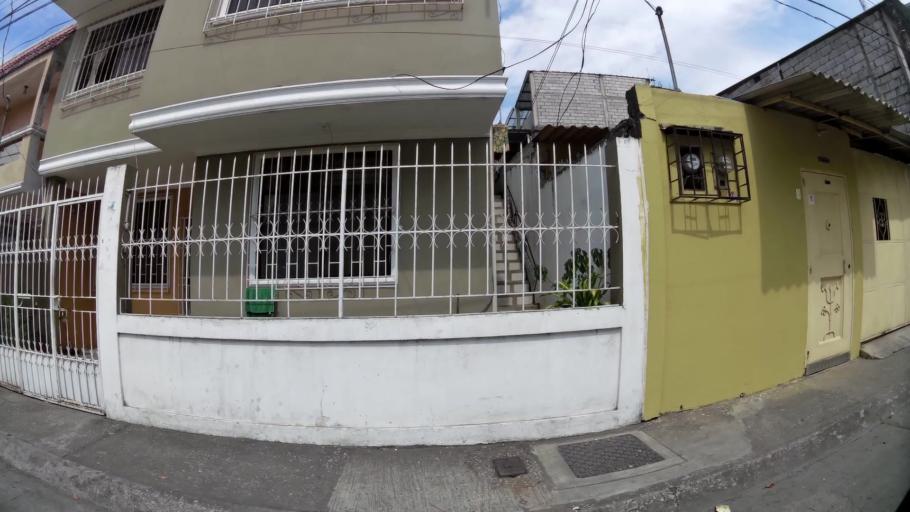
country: EC
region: Guayas
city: Eloy Alfaro
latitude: -2.1232
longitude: -79.8998
